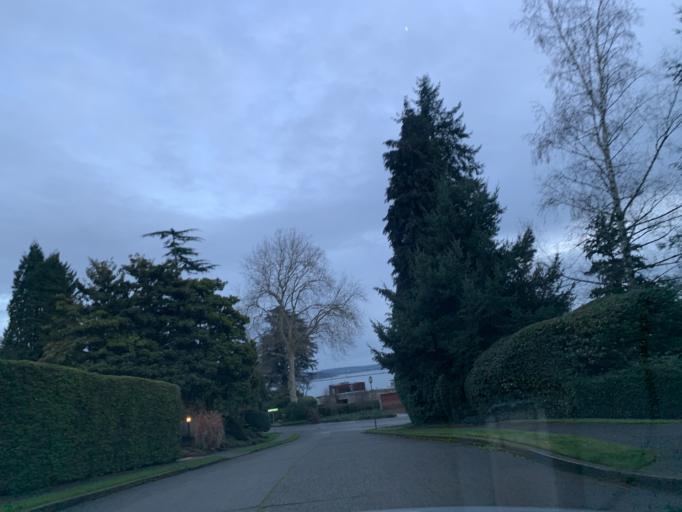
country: US
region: Washington
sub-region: King County
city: Yarrow Point
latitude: 47.6677
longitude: -122.2633
